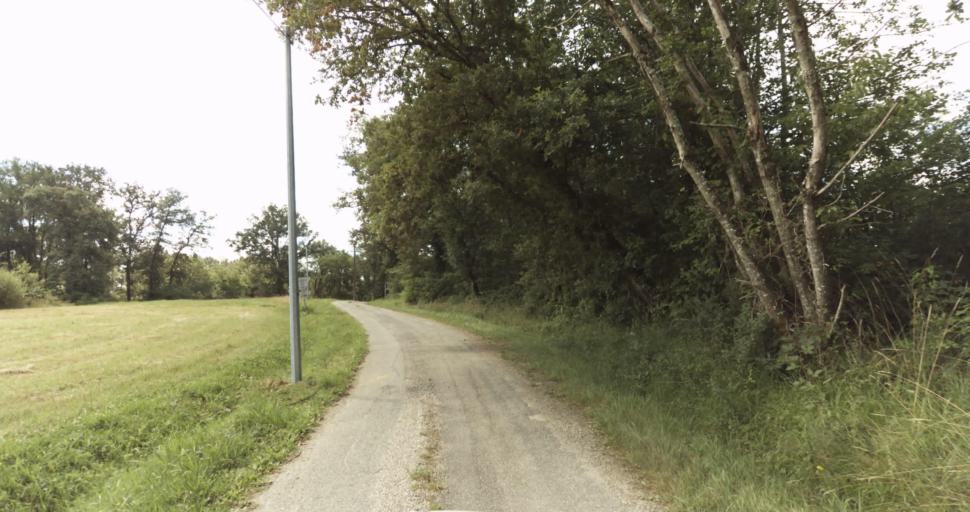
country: FR
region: Aquitaine
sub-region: Departement de la Gironde
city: Bazas
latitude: 44.4670
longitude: -0.1749
